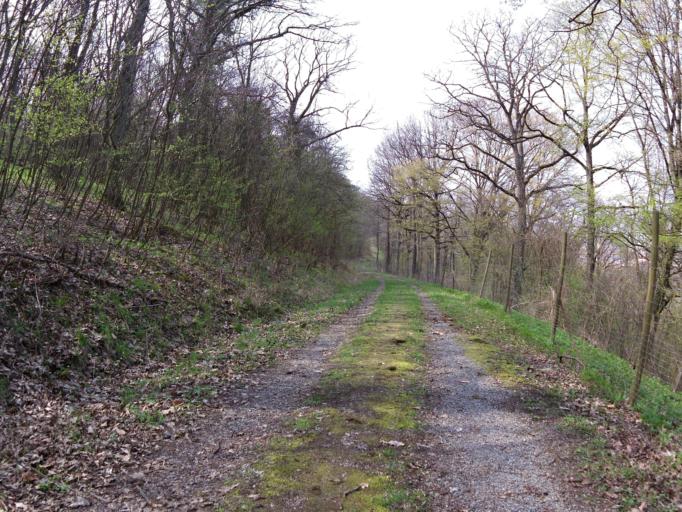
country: DE
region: Bavaria
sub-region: Regierungsbezirk Unterfranken
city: Gerbrunn
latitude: 49.7837
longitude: 10.0136
